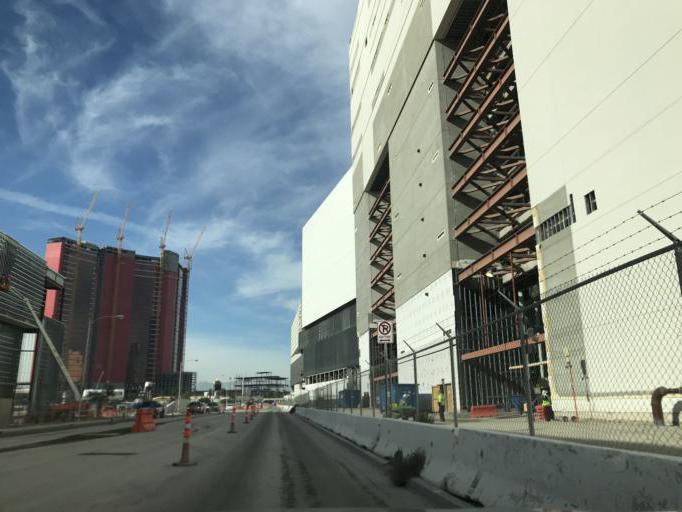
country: US
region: Nevada
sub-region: Clark County
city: Winchester
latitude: 36.1363
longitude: -115.1576
